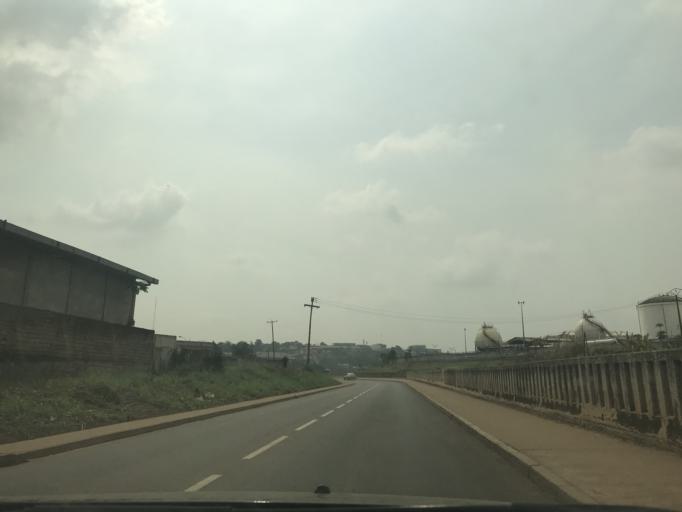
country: CM
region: Centre
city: Yaounde
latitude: 3.8357
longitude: 11.5138
